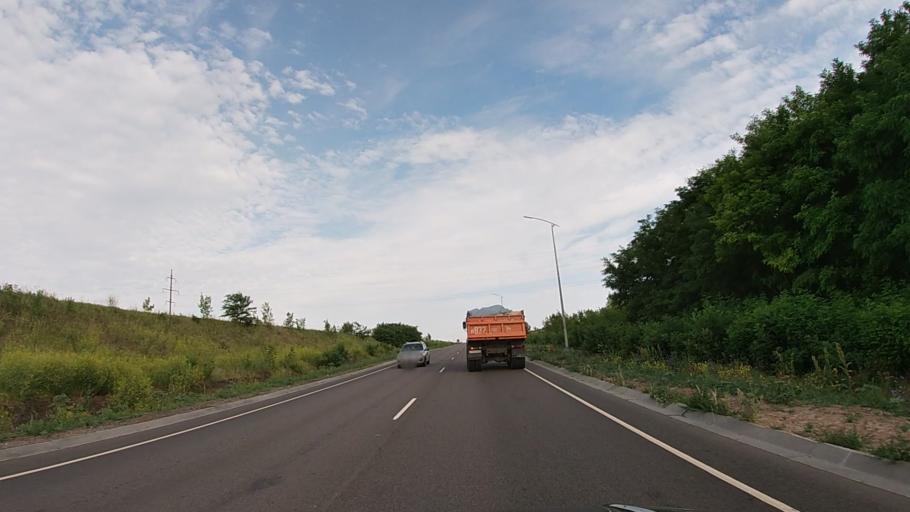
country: RU
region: Belgorod
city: Severnyy
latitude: 50.6699
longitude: 36.4863
